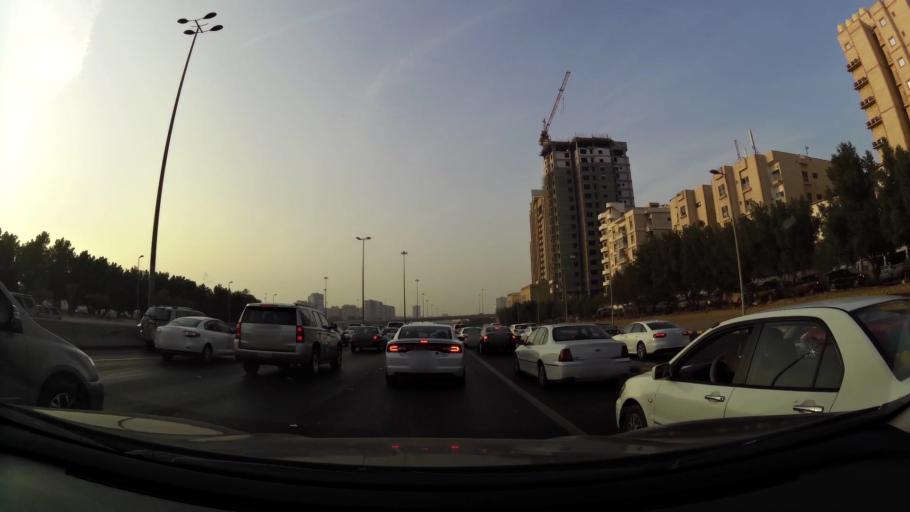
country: KW
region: Muhafazat Hawalli
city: Hawalli
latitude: 29.3271
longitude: 48.0429
